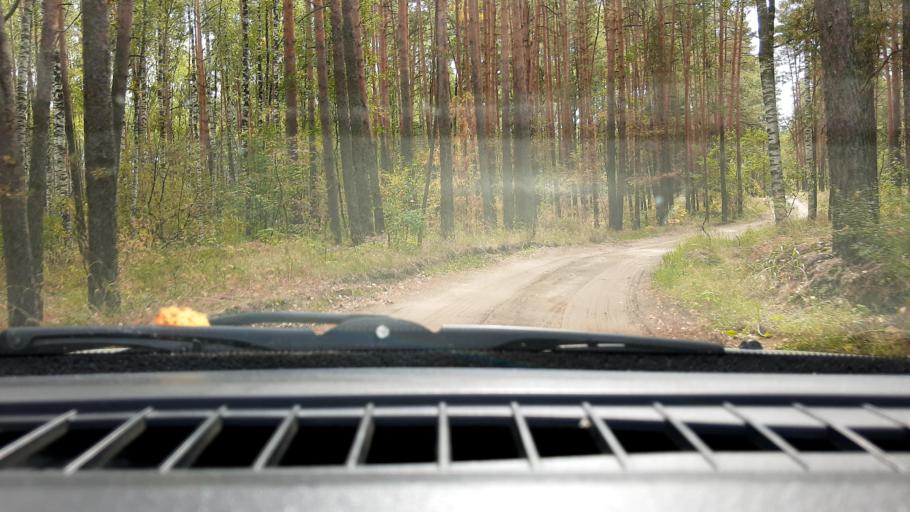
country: RU
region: Nizjnij Novgorod
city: Gorbatovka
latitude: 56.3222
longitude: 43.6925
